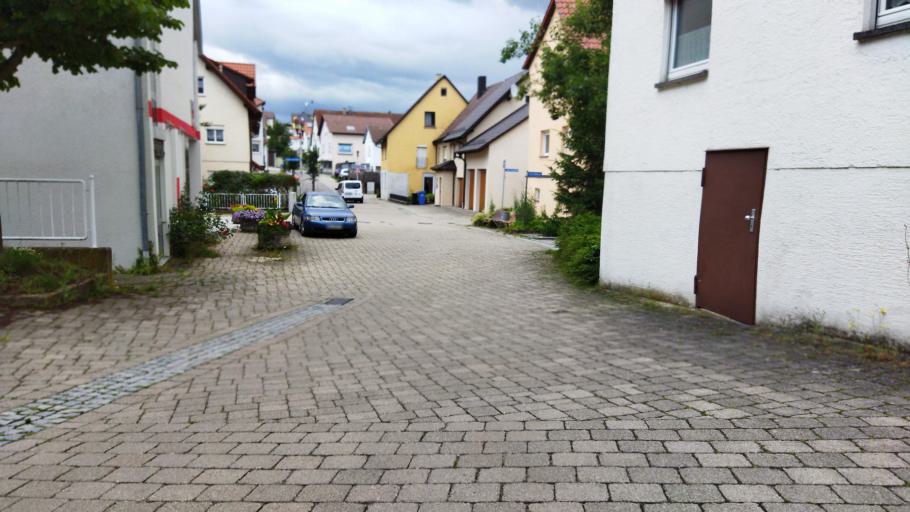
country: DE
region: Baden-Wuerttemberg
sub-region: Regierungsbezirk Stuttgart
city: Massenbachhausen
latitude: 49.2091
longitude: 9.0590
